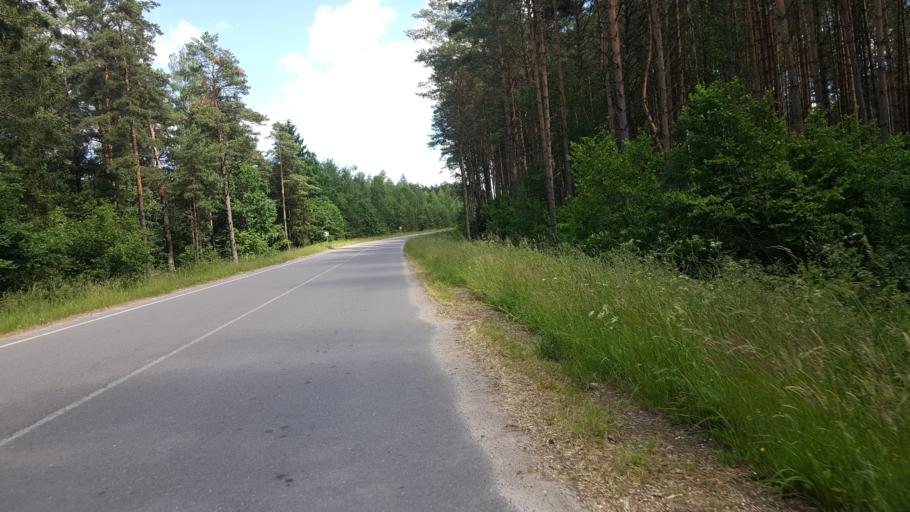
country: PL
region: Podlasie
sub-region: Powiat hajnowski
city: Czeremcha
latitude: 52.5437
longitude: 23.5049
